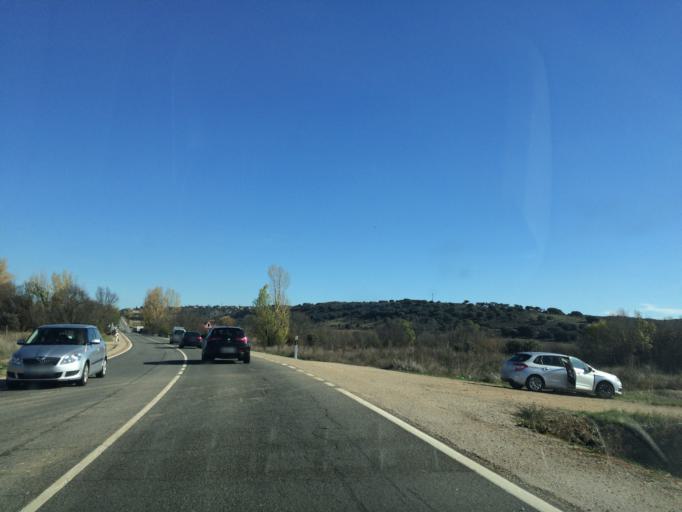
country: ES
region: Madrid
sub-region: Provincia de Madrid
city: Venturada
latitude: 40.7832
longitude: -3.6321
